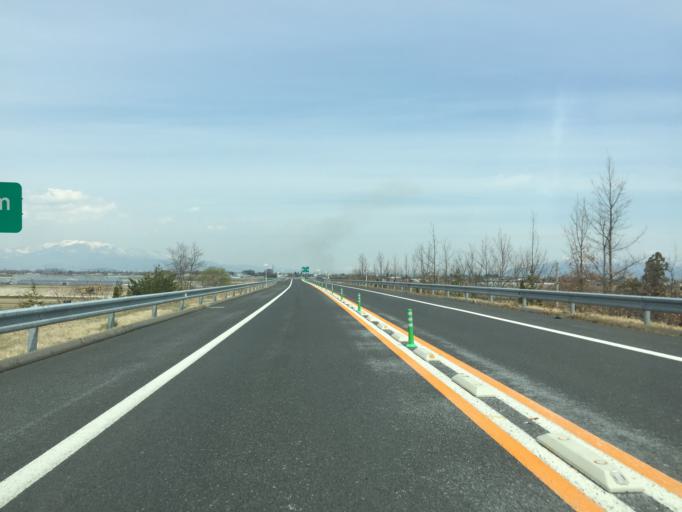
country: JP
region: Yamagata
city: Yamagata-shi
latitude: 38.2850
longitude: 140.2986
